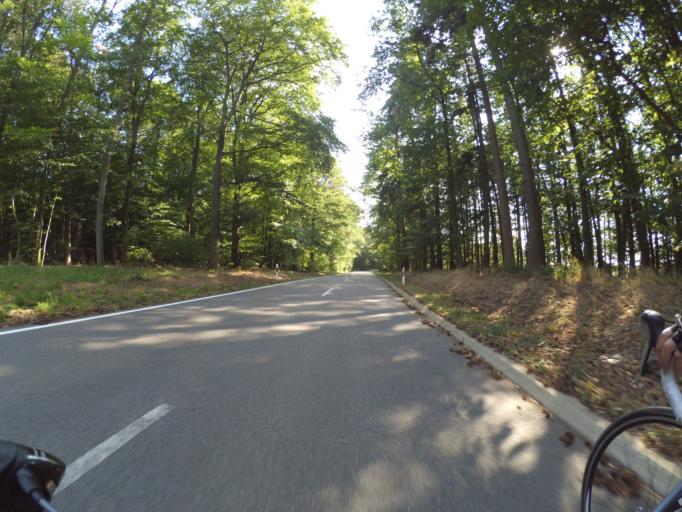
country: DE
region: Rheinland-Pfalz
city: Burgen
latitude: 49.8533
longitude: 6.9789
